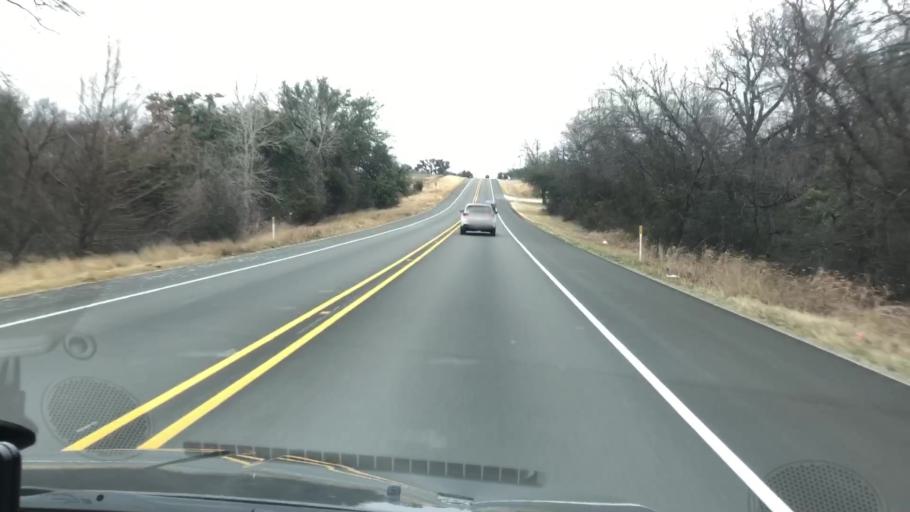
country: US
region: Texas
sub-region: Erath County
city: Stephenville
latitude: 32.3147
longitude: -98.1833
